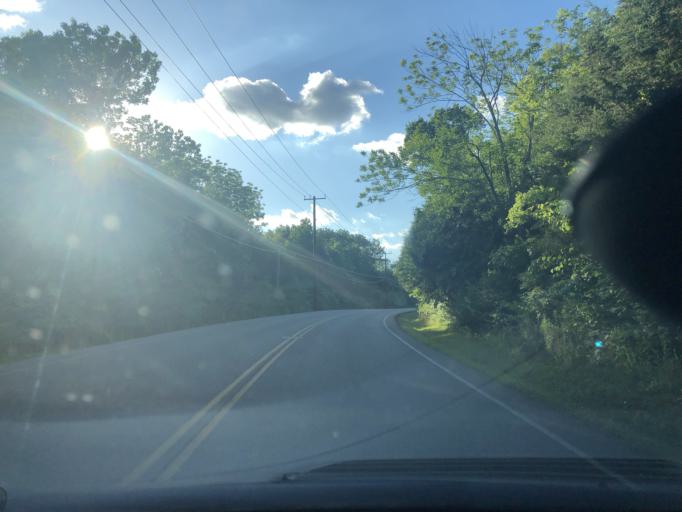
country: US
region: Tennessee
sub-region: Davidson County
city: Forest Hills
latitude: 36.0614
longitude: -86.8379
